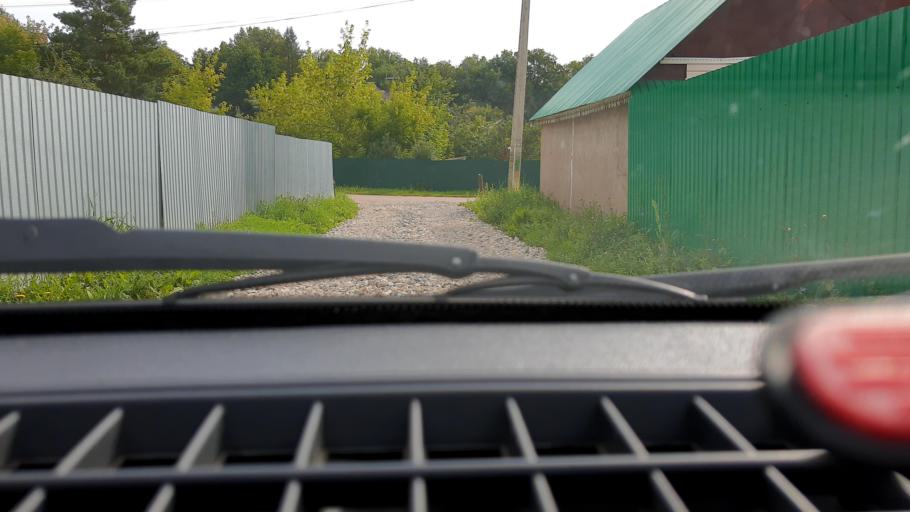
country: RU
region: Bashkortostan
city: Avdon
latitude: 54.6138
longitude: 55.6297
